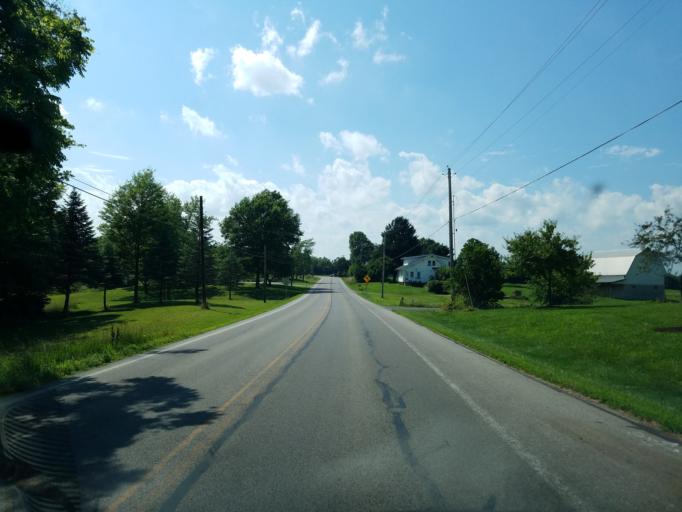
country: US
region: Ohio
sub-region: Ashland County
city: Ashland
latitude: 40.8803
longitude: -82.3423
